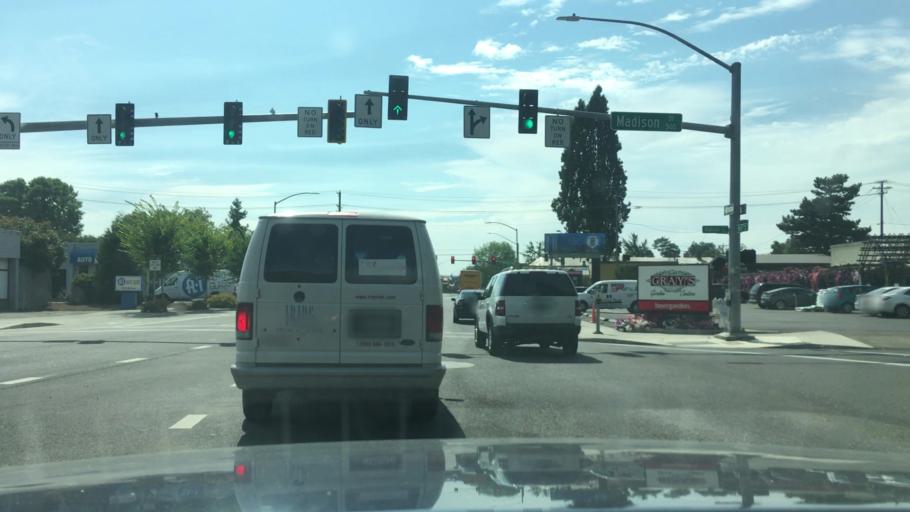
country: US
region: Oregon
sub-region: Lane County
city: Eugene
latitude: 44.0533
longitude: -123.1032
